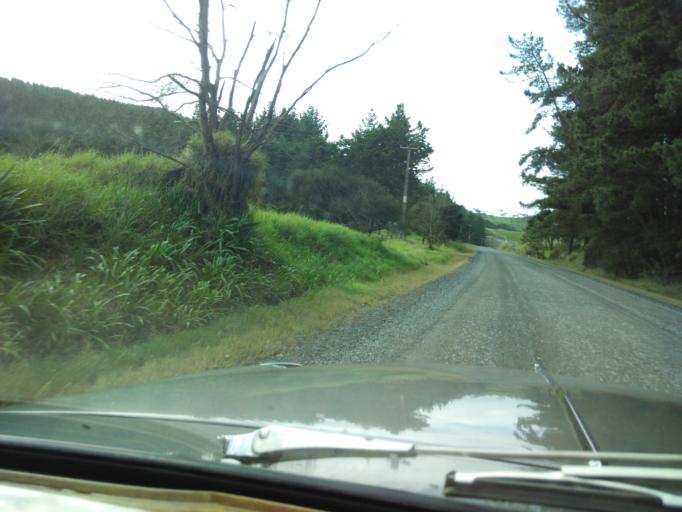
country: NZ
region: Auckland
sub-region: Auckland
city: Wellsford
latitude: -36.3510
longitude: 174.3392
